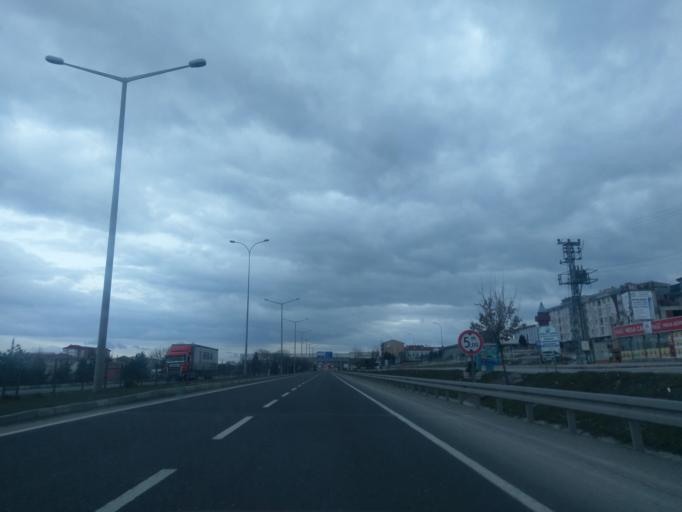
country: TR
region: Kuetahya
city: Kutahya
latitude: 39.3873
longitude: 30.0397
